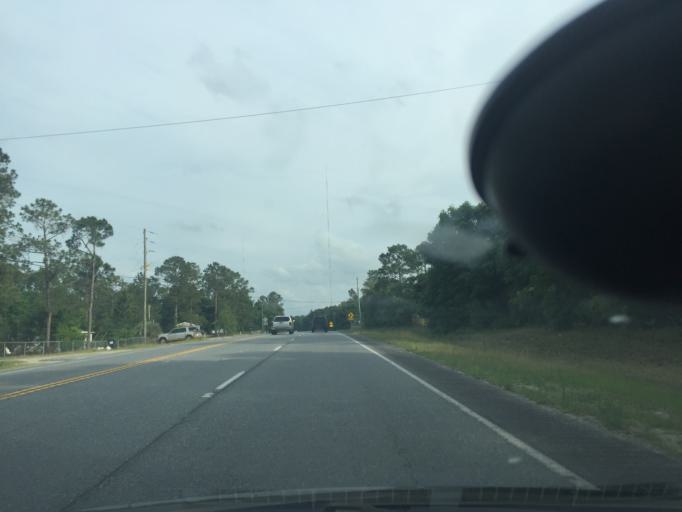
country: US
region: Georgia
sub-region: Chatham County
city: Bloomingdale
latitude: 32.0673
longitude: -81.3578
